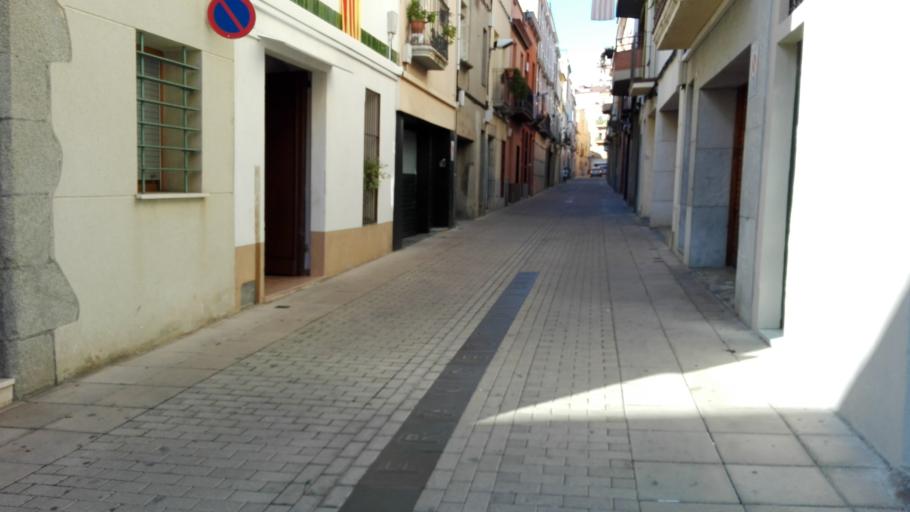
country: ES
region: Catalonia
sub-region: Provincia de Barcelona
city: Mataro
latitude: 41.5372
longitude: 2.4480
